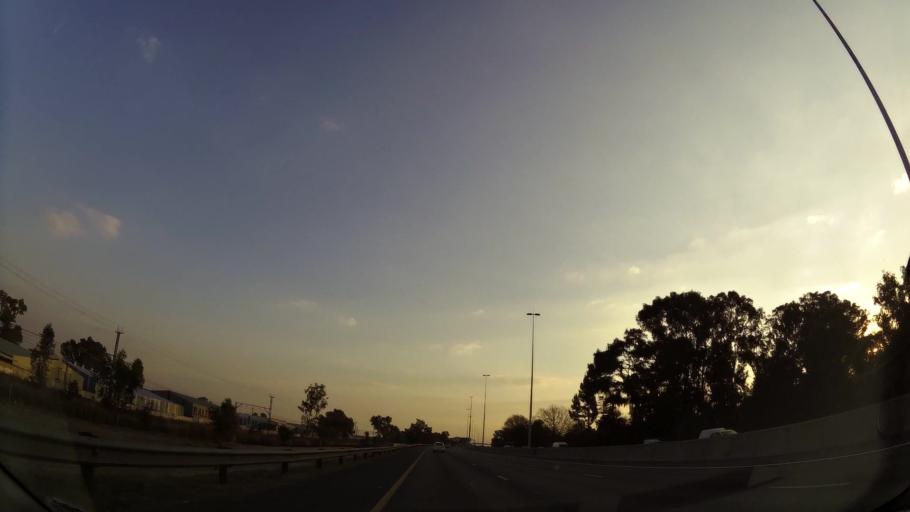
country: ZA
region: Gauteng
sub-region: Ekurhuleni Metropolitan Municipality
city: Benoni
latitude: -26.1704
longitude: 28.3495
